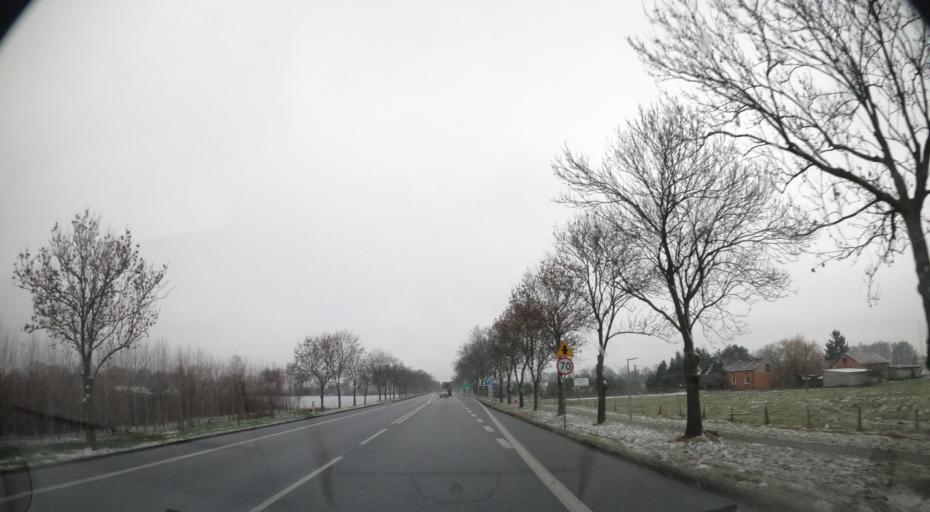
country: PL
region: Masovian Voivodeship
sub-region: Powiat sochaczewski
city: Sochaczew
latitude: 52.2223
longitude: 20.3164
